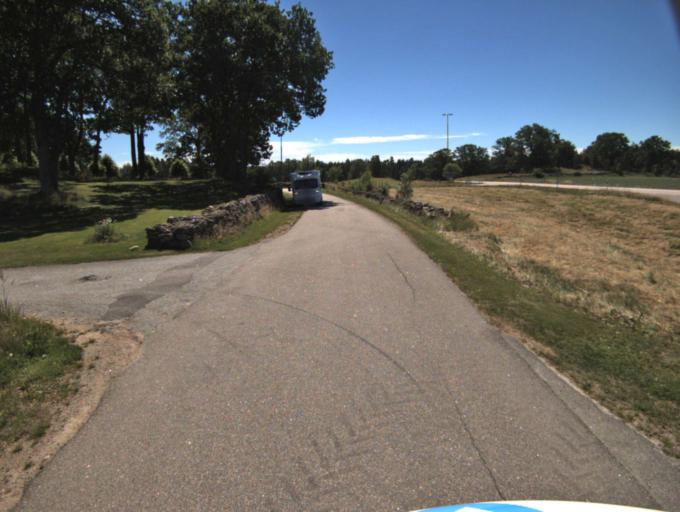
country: SE
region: Vaestra Goetaland
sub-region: Ulricehamns Kommun
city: Ulricehamn
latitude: 57.6602
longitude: 13.4316
